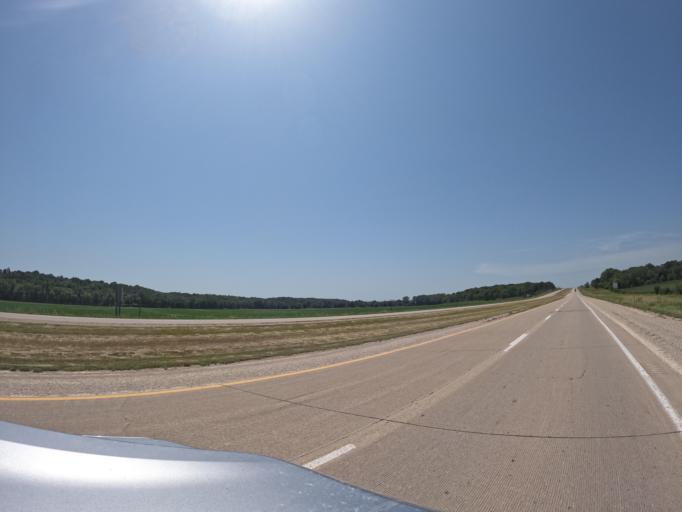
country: US
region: Iowa
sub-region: Henry County
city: Mount Pleasant
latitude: 40.9719
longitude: -91.6471
